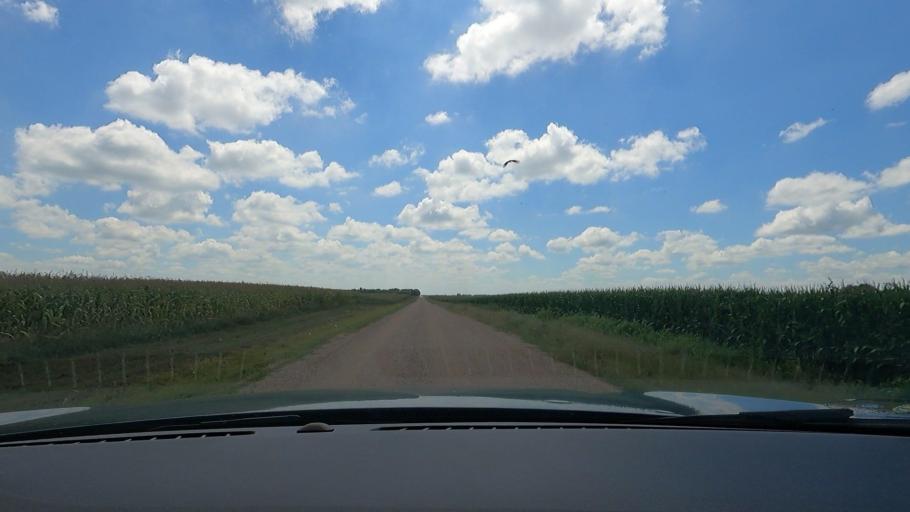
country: US
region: Nebraska
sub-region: Saunders County
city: Wahoo
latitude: 41.2748
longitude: -96.5419
